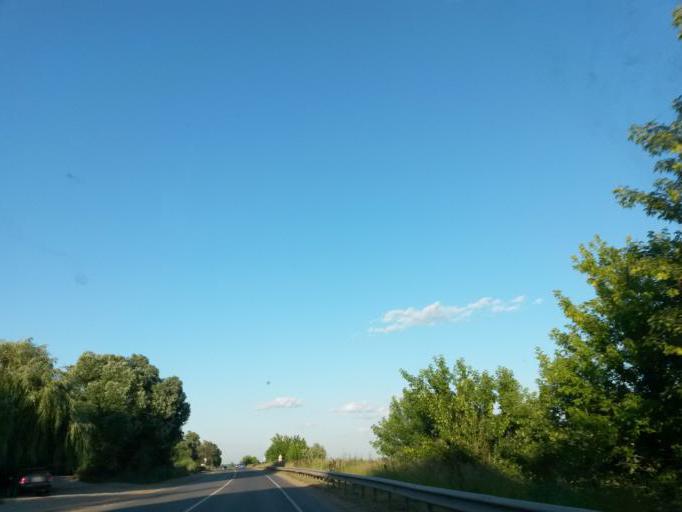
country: RU
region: Moskovskaya
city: Serpukhov
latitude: 54.8933
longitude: 37.3178
